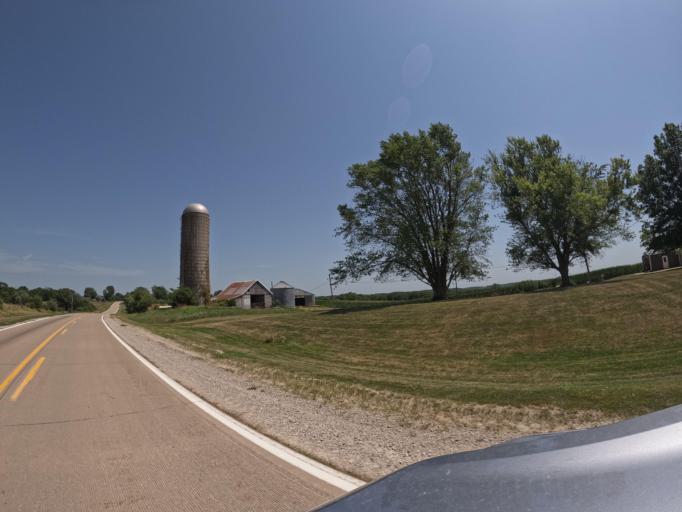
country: US
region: Iowa
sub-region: Henry County
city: Mount Pleasant
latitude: 40.9878
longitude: -91.6474
